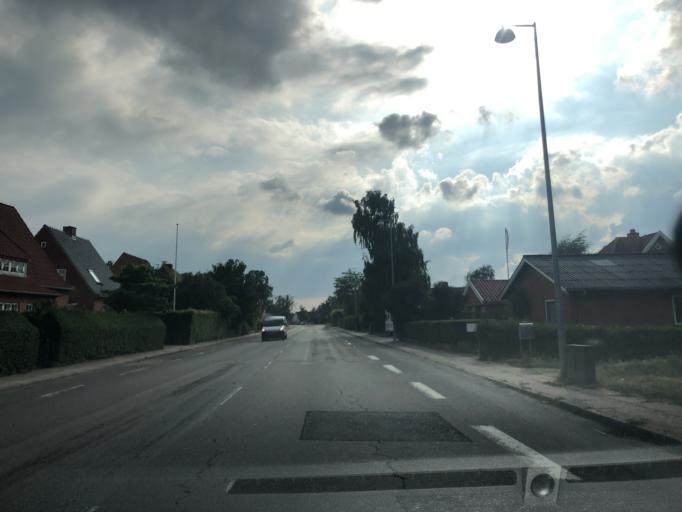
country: DK
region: Zealand
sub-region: Faxe Kommune
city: Haslev
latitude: 55.3185
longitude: 11.9693
